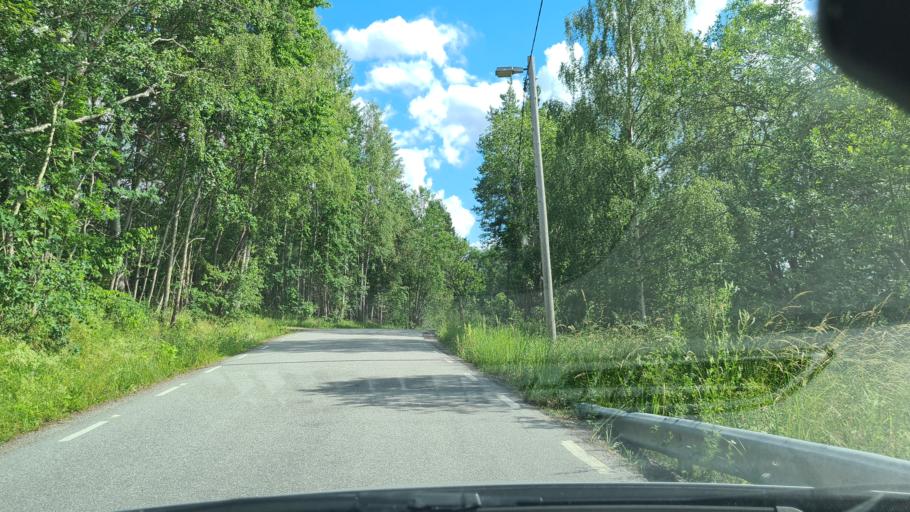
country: SE
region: Stockholm
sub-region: Vaxholms Kommun
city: Vaxholm
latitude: 59.4062
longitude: 18.3627
